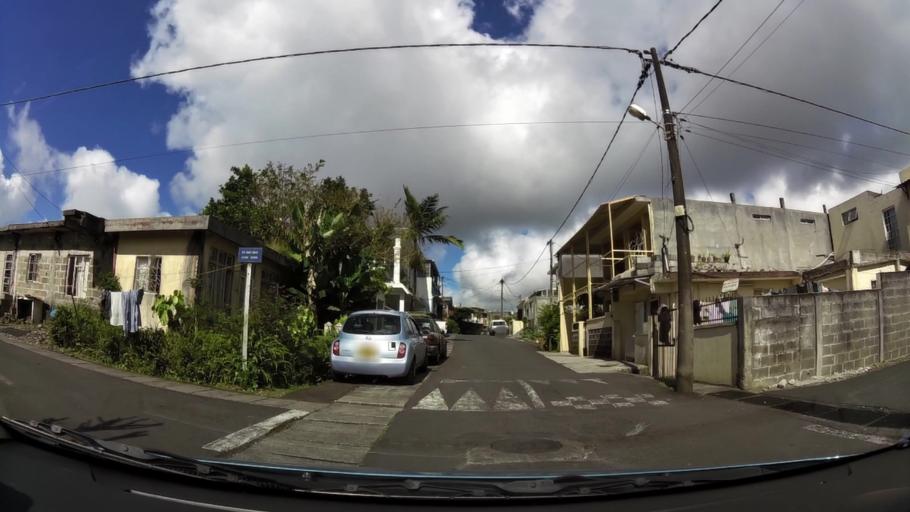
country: MU
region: Plaines Wilhems
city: Curepipe
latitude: -20.3309
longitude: 57.5249
